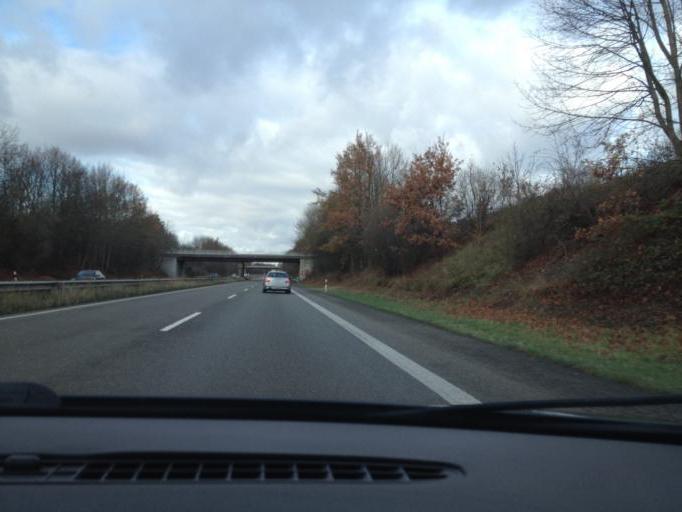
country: DE
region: Rheinland-Pfalz
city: Westheim
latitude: 49.2447
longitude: 8.3326
